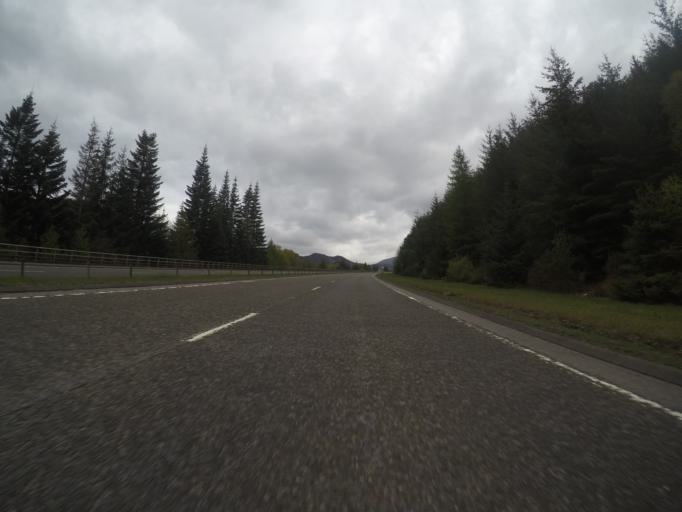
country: GB
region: Scotland
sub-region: Perth and Kinross
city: Pitlochry
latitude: 56.7289
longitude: -3.7735
